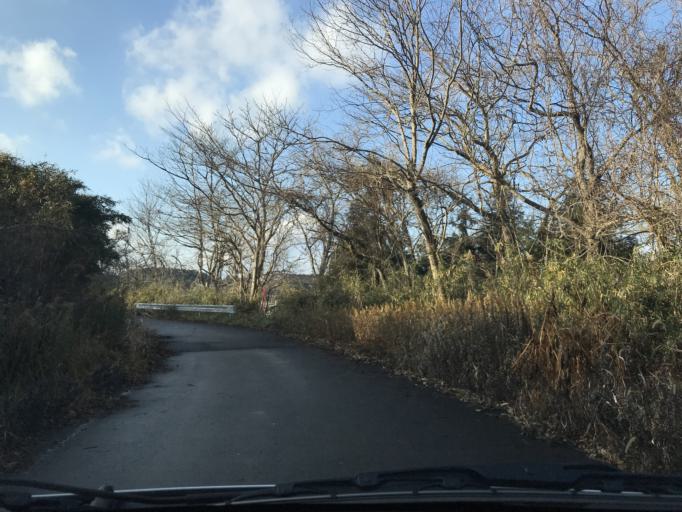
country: JP
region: Miyagi
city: Wakuya
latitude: 38.6883
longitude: 141.1133
